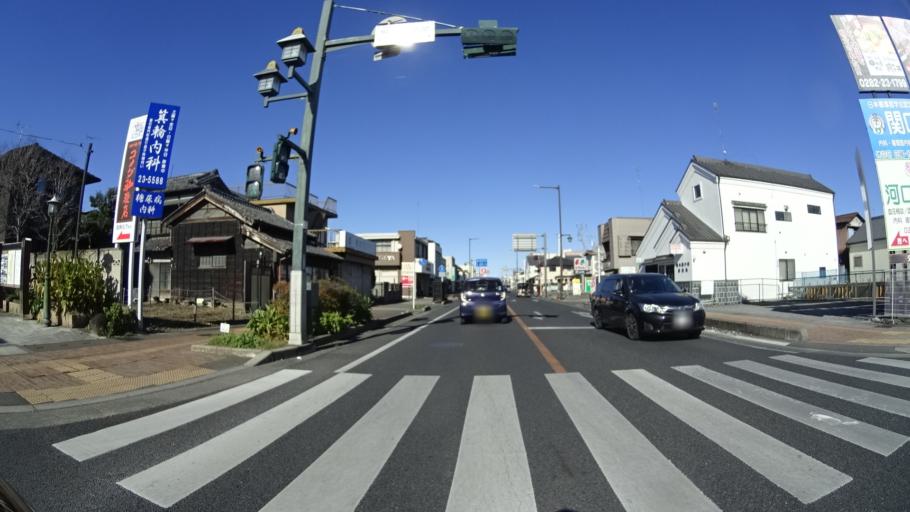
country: JP
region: Tochigi
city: Tochigi
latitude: 36.3841
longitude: 139.7350
